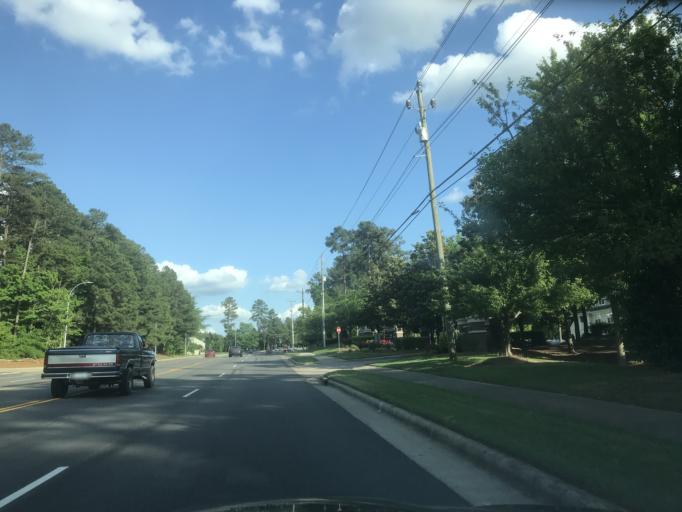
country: US
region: North Carolina
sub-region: Wake County
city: Morrisville
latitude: 35.8128
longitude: -78.8188
